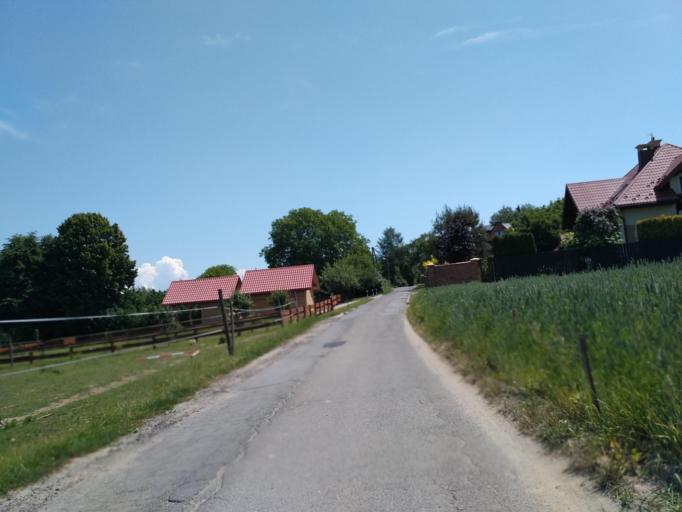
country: PL
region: Subcarpathian Voivodeship
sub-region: Powiat krosnienski
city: Korczyna
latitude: 49.7123
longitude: 21.7855
